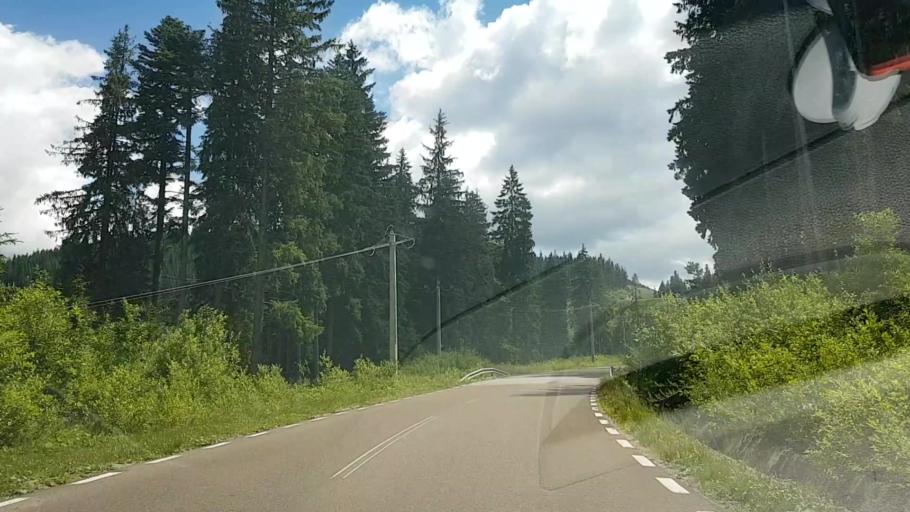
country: RO
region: Suceava
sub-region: Comuna Sadova
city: Sadova
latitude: 47.4605
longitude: 25.5143
